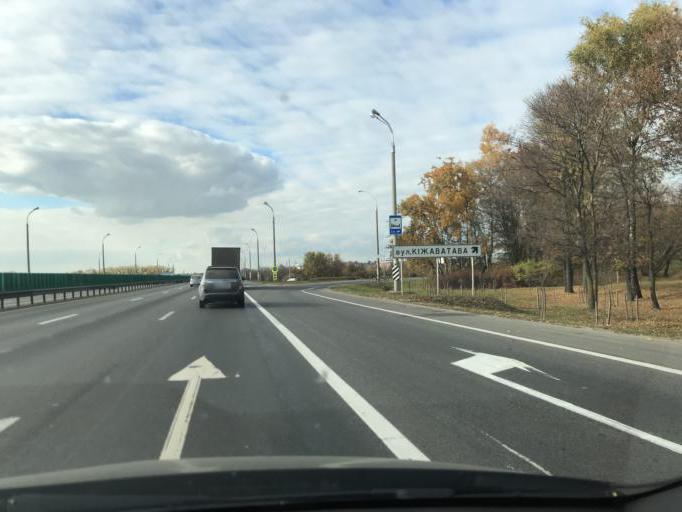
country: BY
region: Minsk
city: Syenitsa
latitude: 53.8350
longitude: 27.5386
